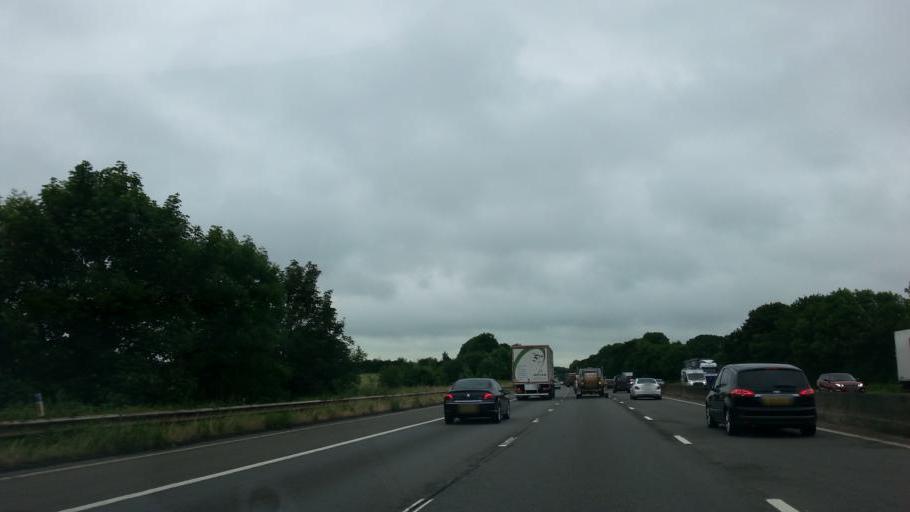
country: GB
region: England
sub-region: Leicestershire
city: Lutterworth
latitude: 52.4600
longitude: -1.1933
